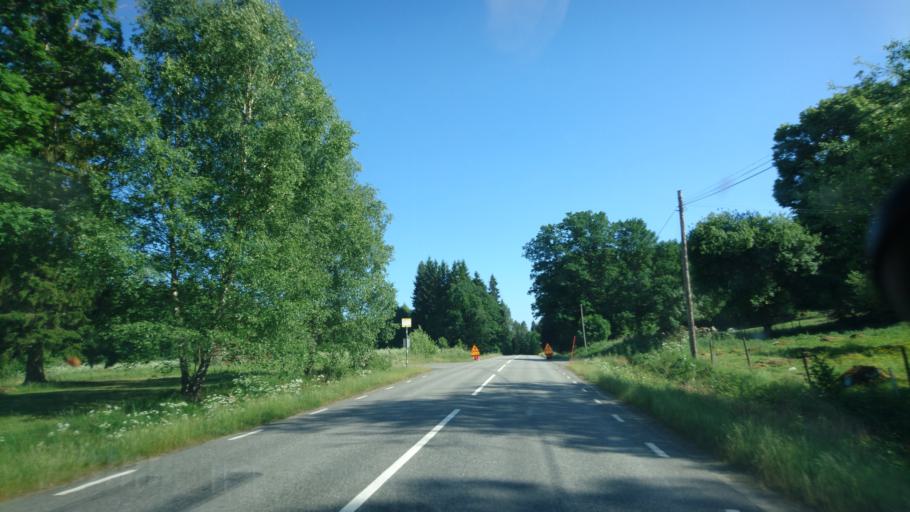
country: SE
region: Skane
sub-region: Osby Kommun
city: Lonsboda
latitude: 56.4215
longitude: 14.2843
